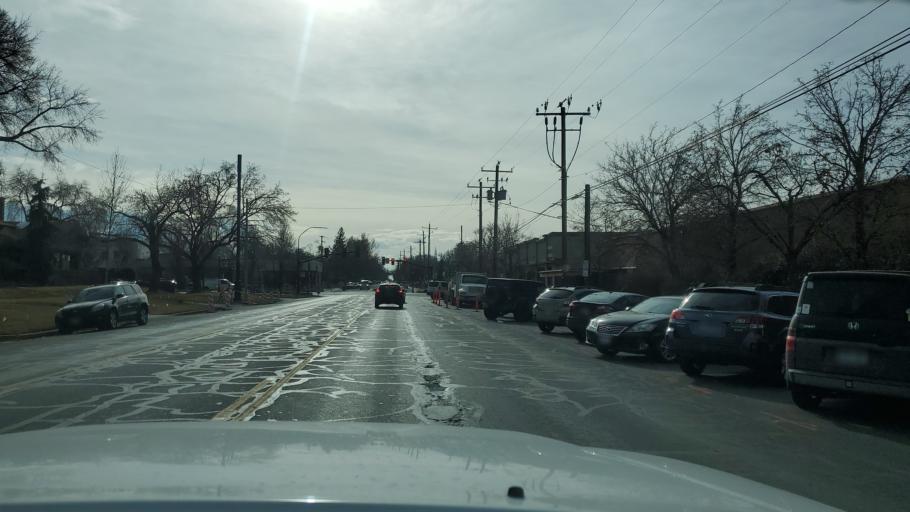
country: US
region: Utah
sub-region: Salt Lake County
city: Salt Lake City
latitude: 40.7509
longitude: -111.8654
